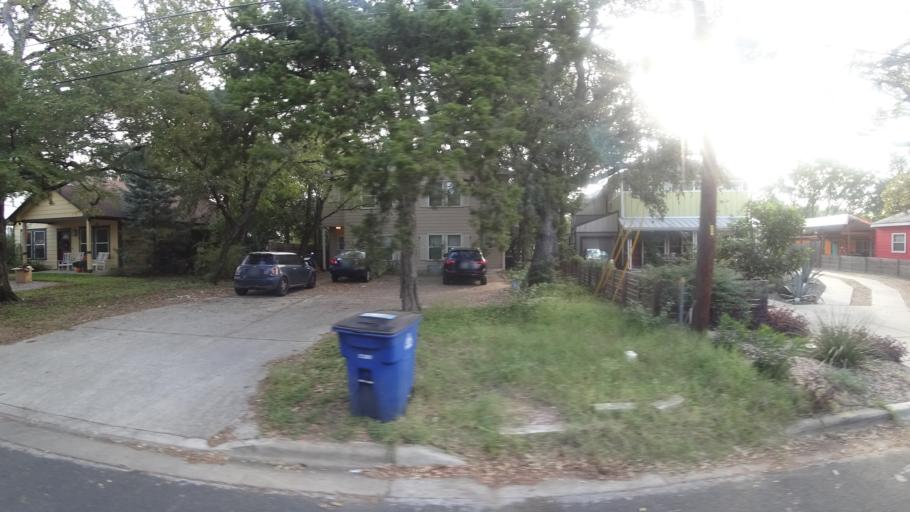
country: US
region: Texas
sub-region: Travis County
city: Austin
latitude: 30.2745
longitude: -97.7057
